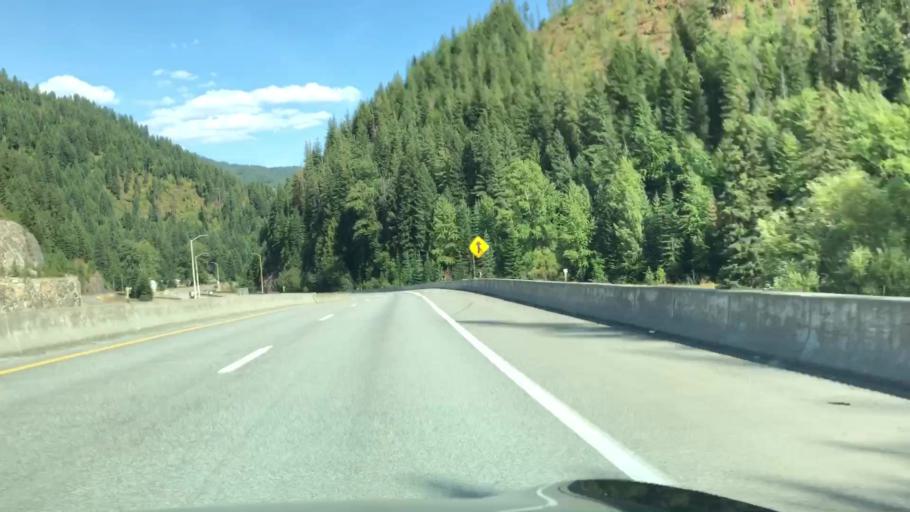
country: US
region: Idaho
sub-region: Shoshone County
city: Wallace
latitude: 47.4729
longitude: -115.9134
